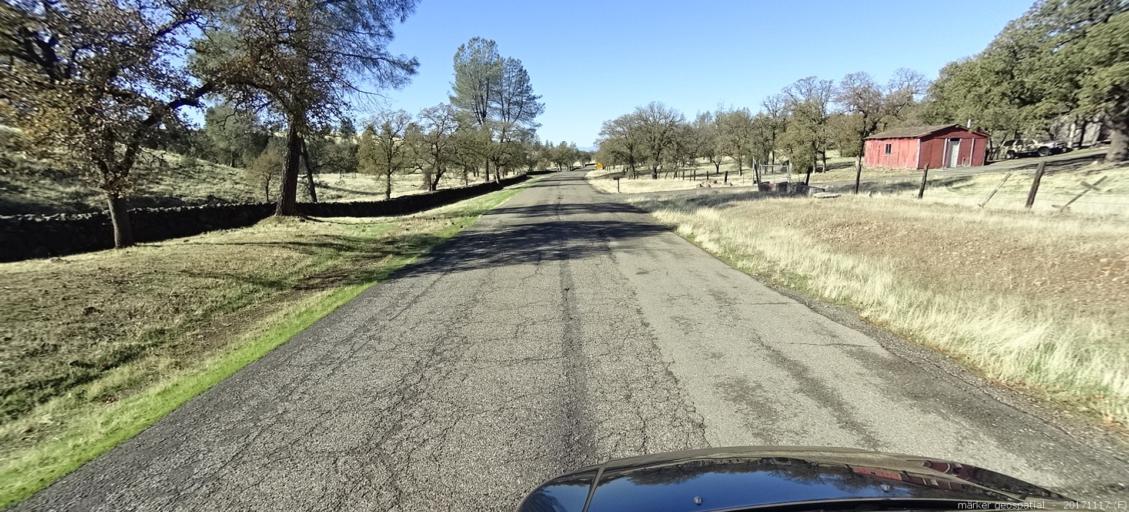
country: US
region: California
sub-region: Shasta County
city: Cottonwood
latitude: 40.4400
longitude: -122.1333
